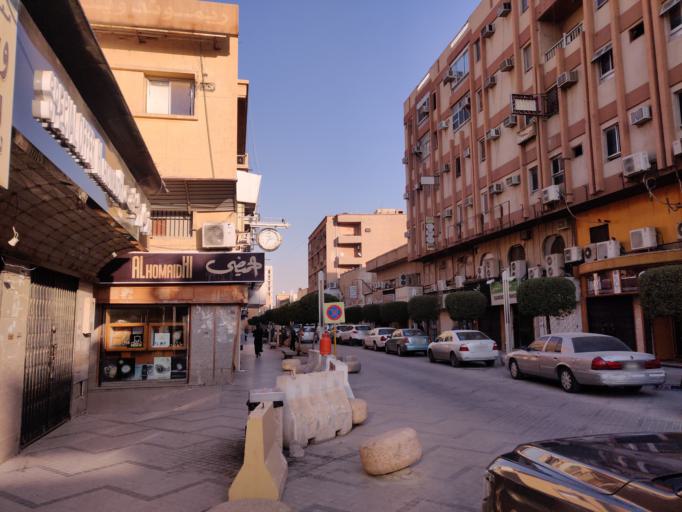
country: SA
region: Ar Riyad
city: Riyadh
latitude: 24.6308
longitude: 46.7140
